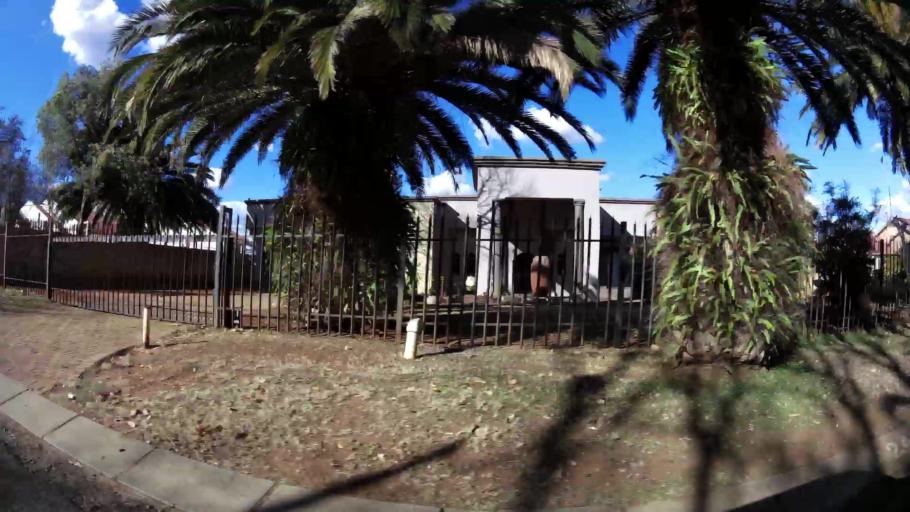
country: ZA
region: North-West
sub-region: Dr Kenneth Kaunda District Municipality
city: Klerksdorp
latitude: -26.8315
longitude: 26.6803
